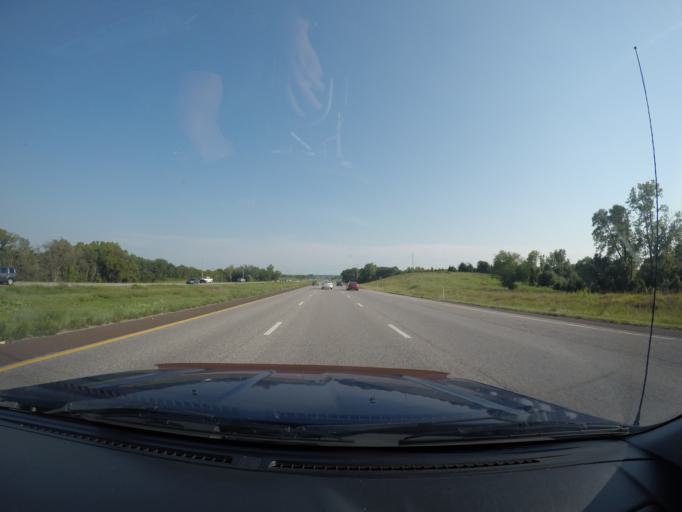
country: US
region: Kansas
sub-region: Wyandotte County
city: Edwardsville
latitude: 39.0823
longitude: -94.7994
